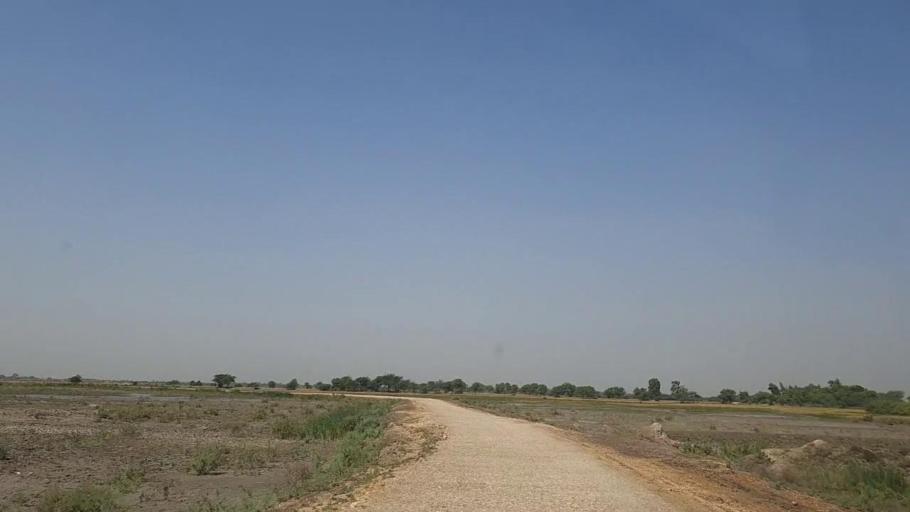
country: PK
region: Sindh
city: Daro Mehar
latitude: 24.7526
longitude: 68.1395
